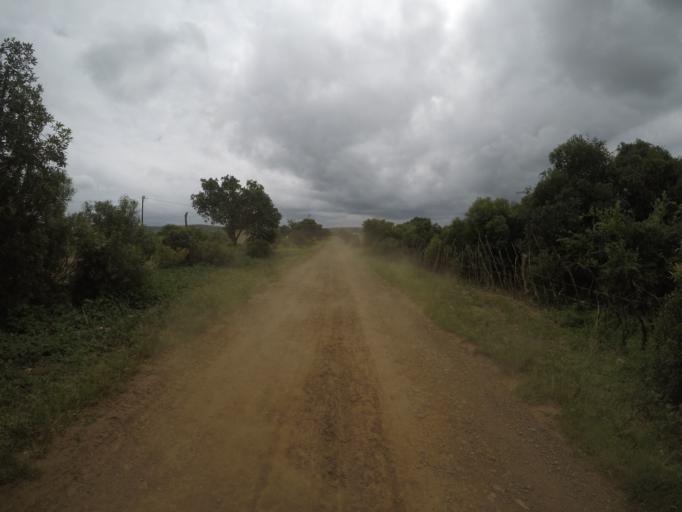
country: ZA
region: KwaZulu-Natal
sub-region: uThungulu District Municipality
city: Empangeni
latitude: -28.6008
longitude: 31.8335
